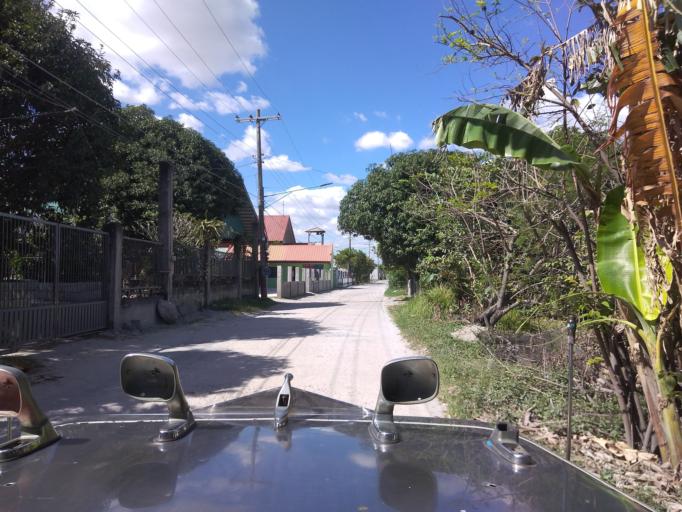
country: PH
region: Central Luzon
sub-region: Province of Pampanga
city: Bacolor
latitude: 15.0110
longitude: 120.6439
